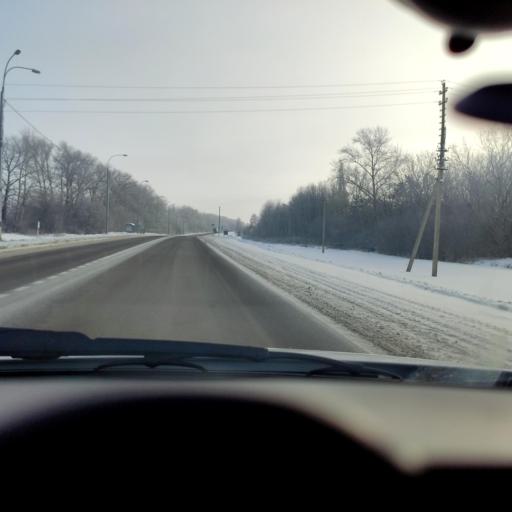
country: RU
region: Kursk
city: Kirovskiy
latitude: 51.6765
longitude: 36.6017
